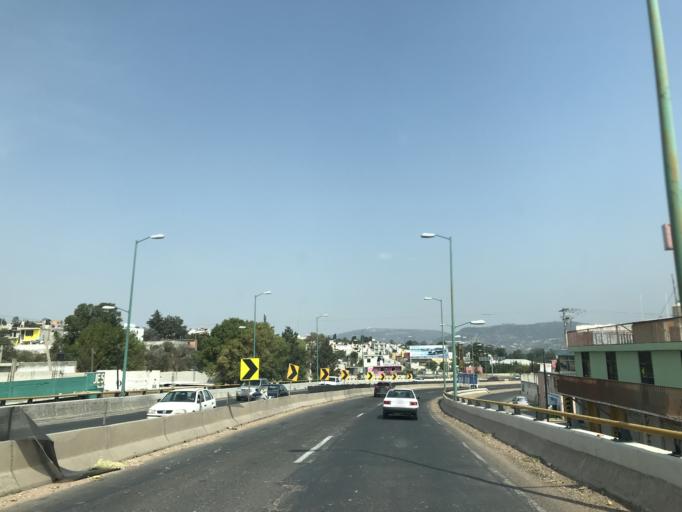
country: MX
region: Tlaxcala
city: Tlaxcala de Xicohtencatl
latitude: 19.3129
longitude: -98.2034
